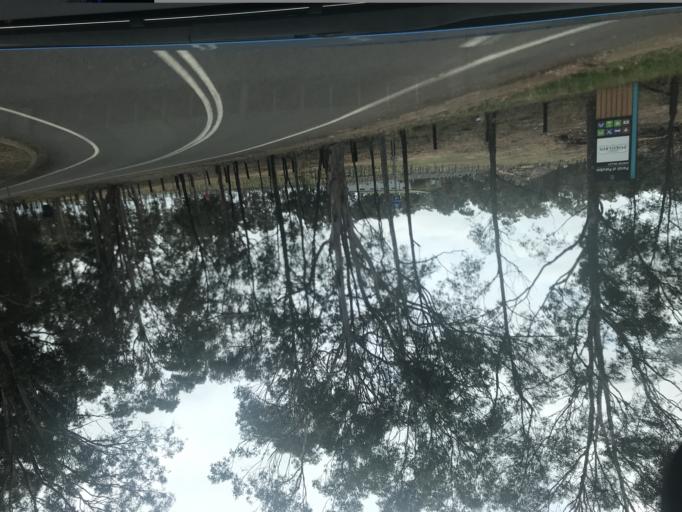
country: AU
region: New South Wales
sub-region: Cessnock
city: Cessnock
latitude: -32.8282
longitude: 151.3226
